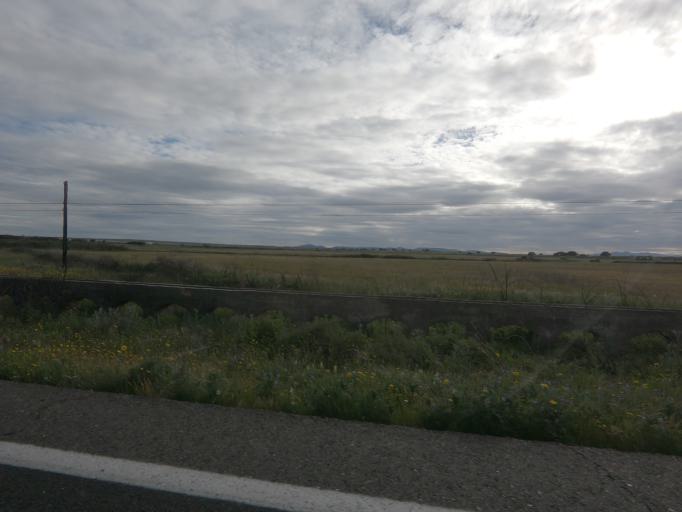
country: ES
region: Extremadura
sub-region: Provincia de Caceres
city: Huelaga
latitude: 40.0446
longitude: -6.6341
